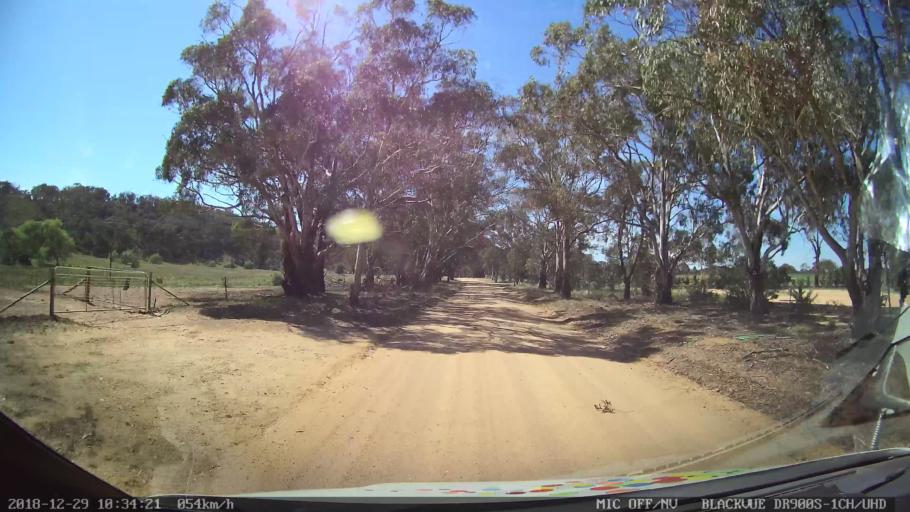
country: AU
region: New South Wales
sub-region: Yass Valley
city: Gundaroo
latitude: -34.9861
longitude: 149.4775
